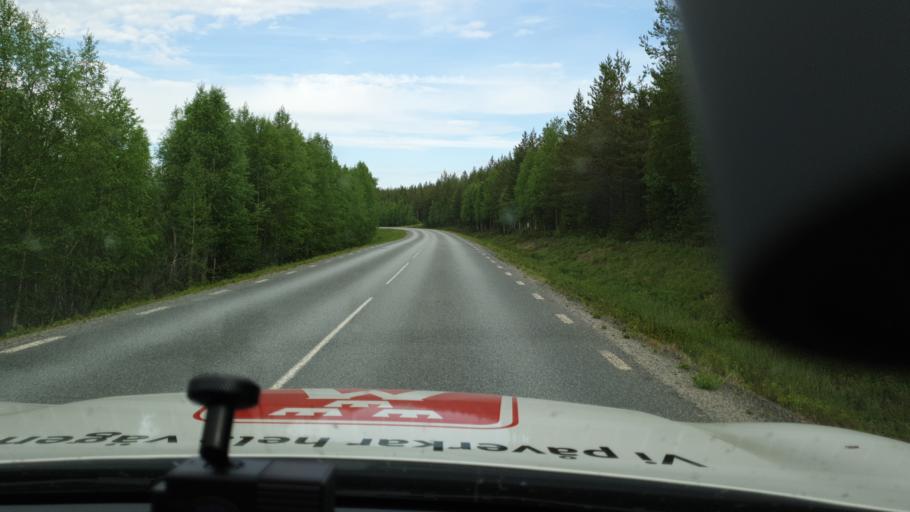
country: SE
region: Vaesterbotten
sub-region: Mala Kommun
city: Mala
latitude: 65.0124
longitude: 18.4532
